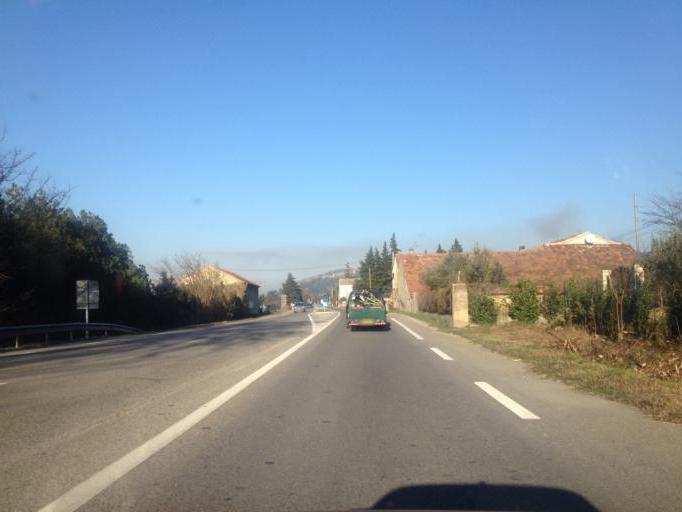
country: FR
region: Provence-Alpes-Cote d'Azur
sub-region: Departement du Vaucluse
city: Mornas
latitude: 44.1911
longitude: 4.7443
